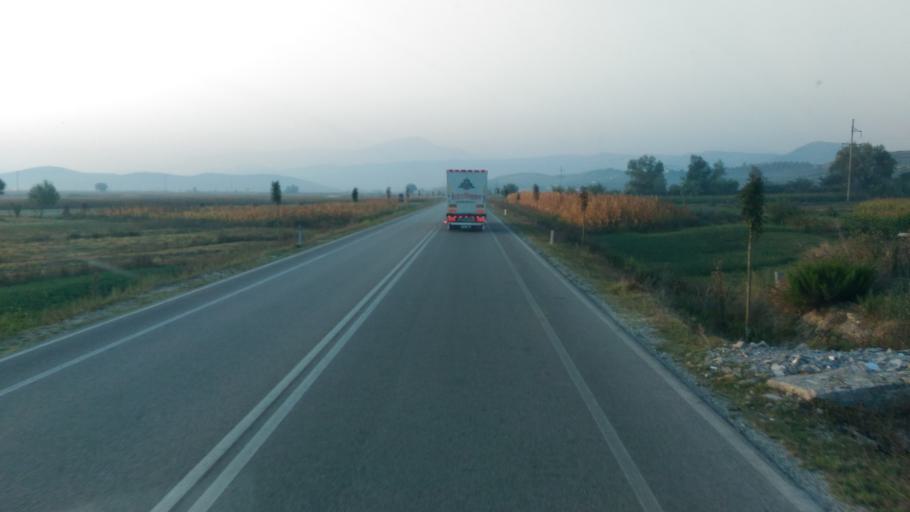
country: AL
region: Fier
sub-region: Rrethi i Fierit
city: Cakran
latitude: 40.5779
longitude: 19.6212
